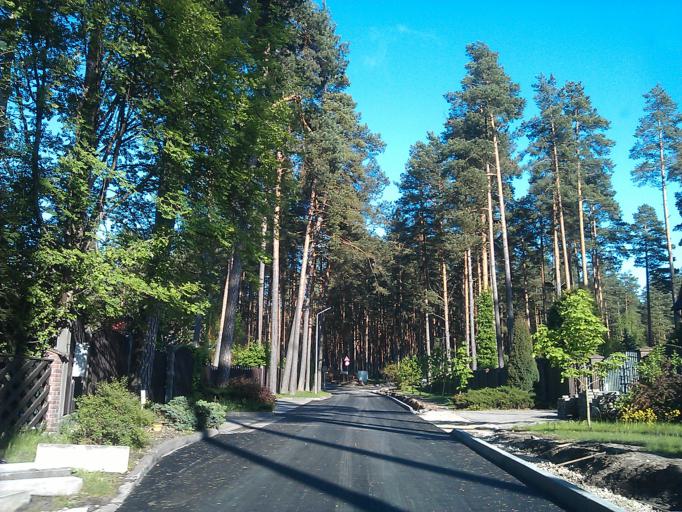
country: LV
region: Riga
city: Bergi
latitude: 57.0159
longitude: 24.2905
